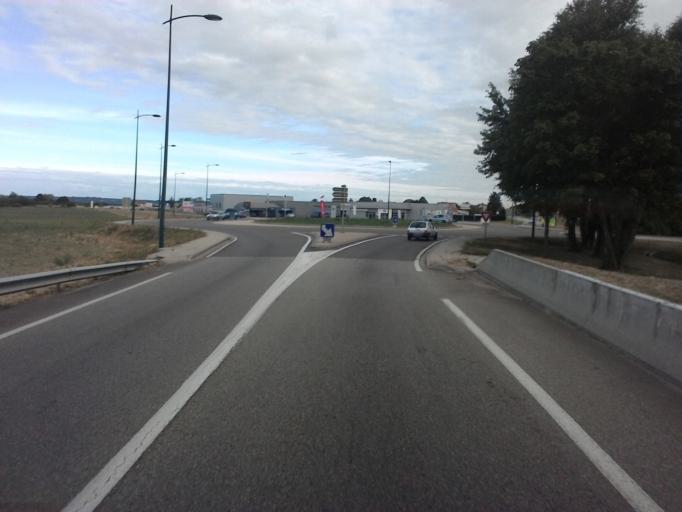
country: FR
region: Rhone-Alpes
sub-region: Departement de l'Ain
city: Saint-Denis-en-Bugey
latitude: 45.9406
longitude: 5.3323
